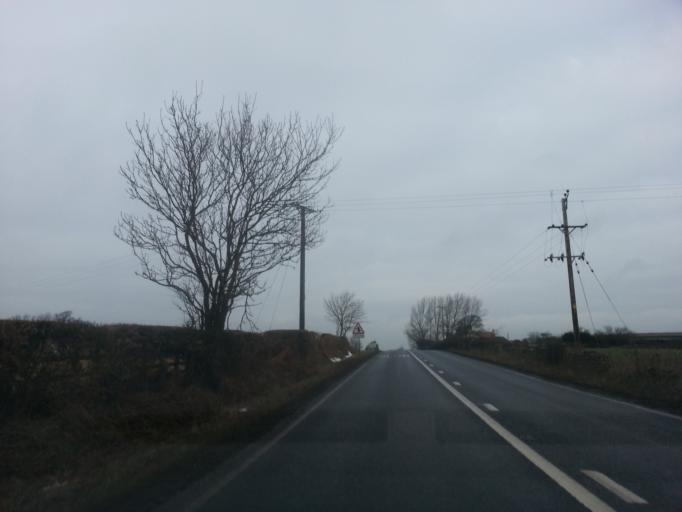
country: GB
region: England
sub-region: Darlington
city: Summerhouse
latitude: 54.6053
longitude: -1.6783
